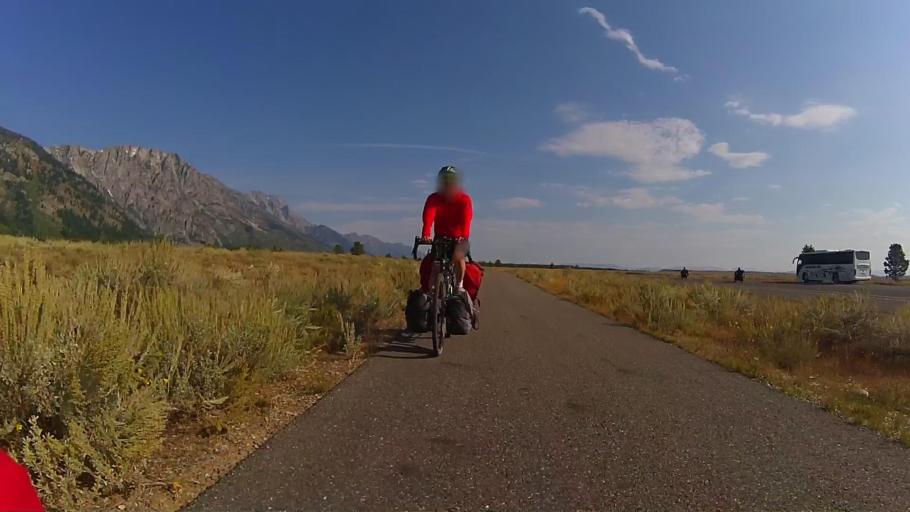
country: US
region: Wyoming
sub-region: Teton County
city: Moose Wilson Road
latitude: 43.7409
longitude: -110.7249
